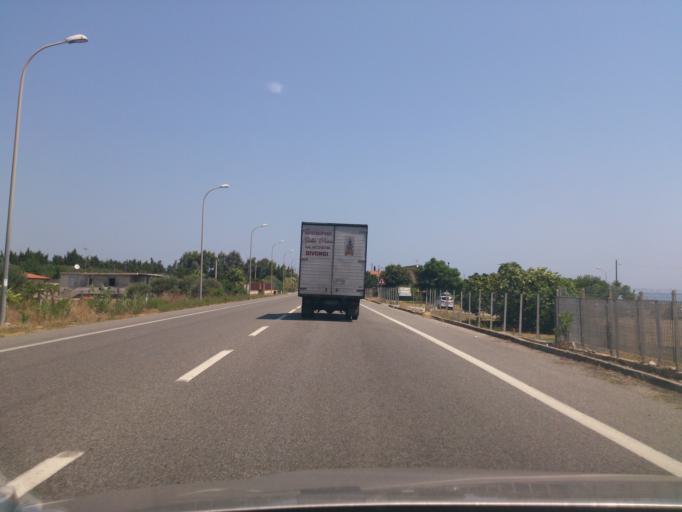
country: IT
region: Calabria
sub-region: Provincia di Reggio Calabria
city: Monasterace Marina
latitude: 38.4151
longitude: 16.5584
